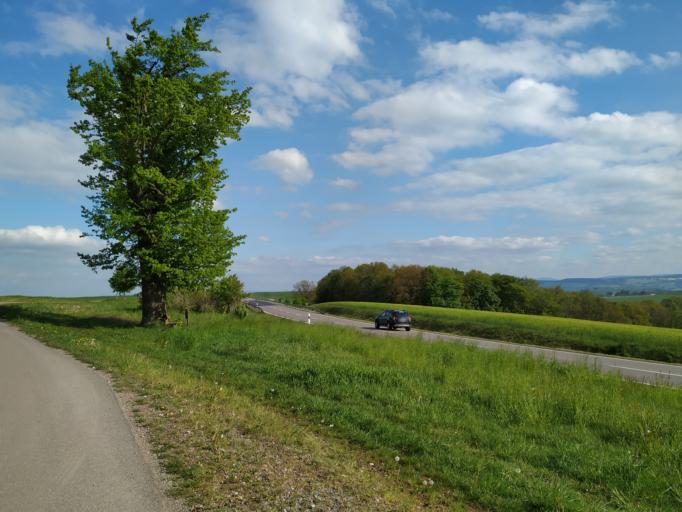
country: DE
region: Saxony
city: Reinsdorf
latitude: 50.7019
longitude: 12.5865
